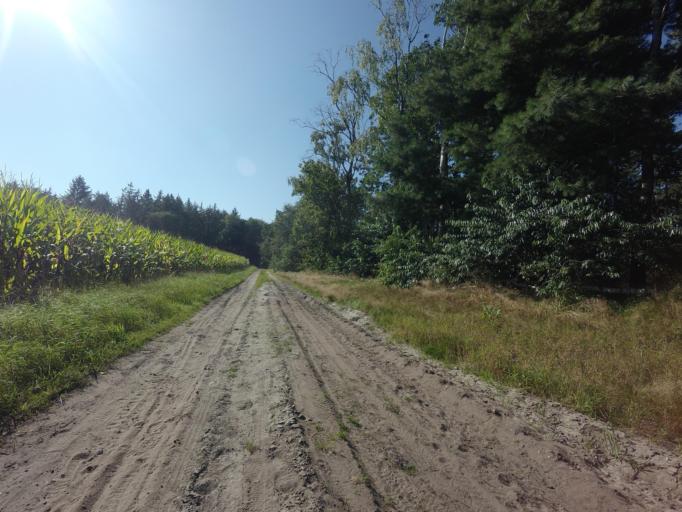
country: DE
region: Lower Saxony
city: Wielen
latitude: 52.5441
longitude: 6.7168
